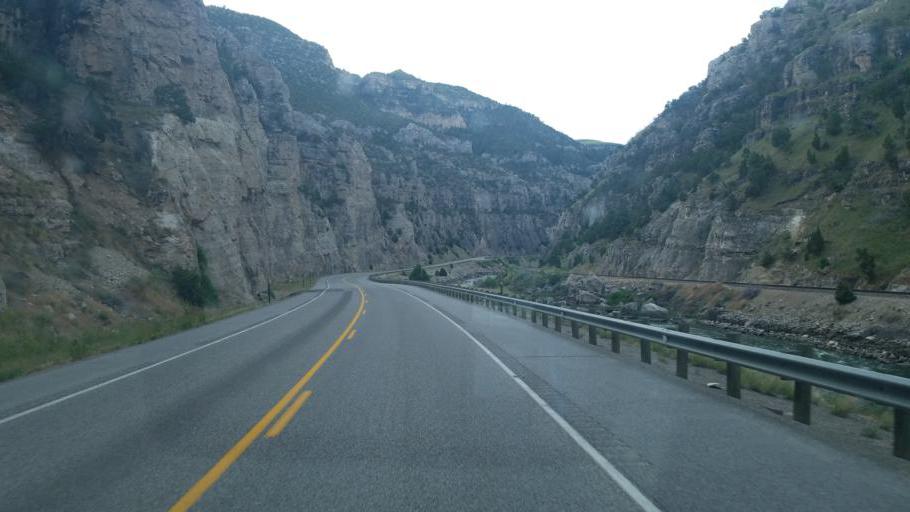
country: US
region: Wyoming
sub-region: Hot Springs County
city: Thermopolis
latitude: 43.5450
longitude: -108.1872
